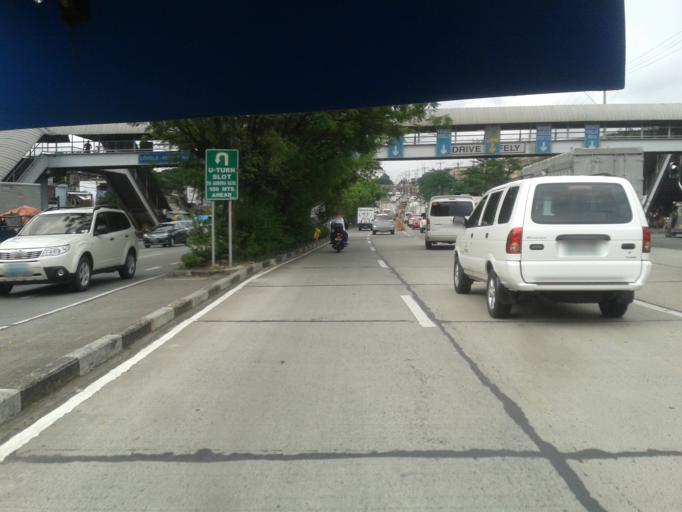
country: PH
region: Metro Manila
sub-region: Quezon City
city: Quezon City
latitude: 14.6466
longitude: 121.0744
